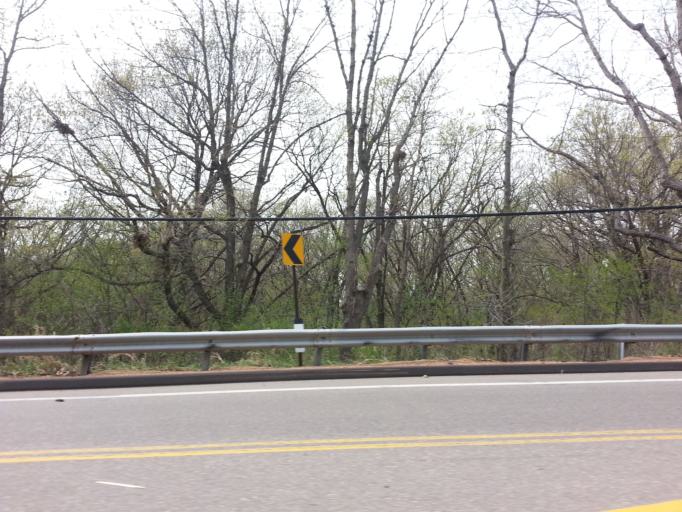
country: US
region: Minnesota
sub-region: Hennepin County
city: Edina
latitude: 44.8494
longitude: -93.3716
